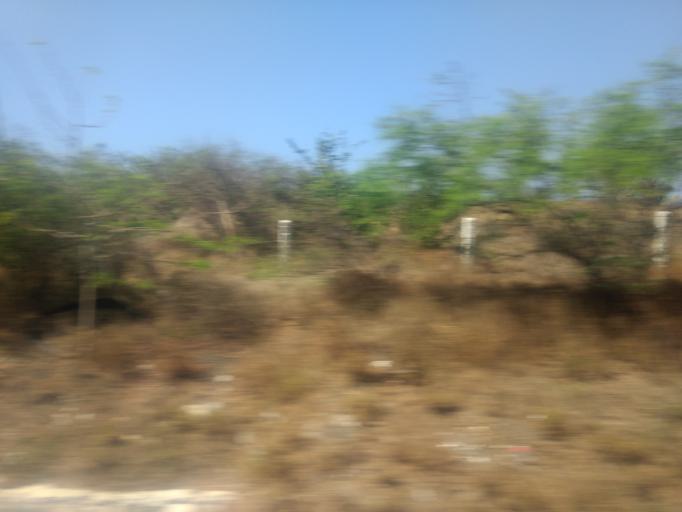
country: MX
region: Colima
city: Armeria
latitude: 18.9500
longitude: -104.1255
